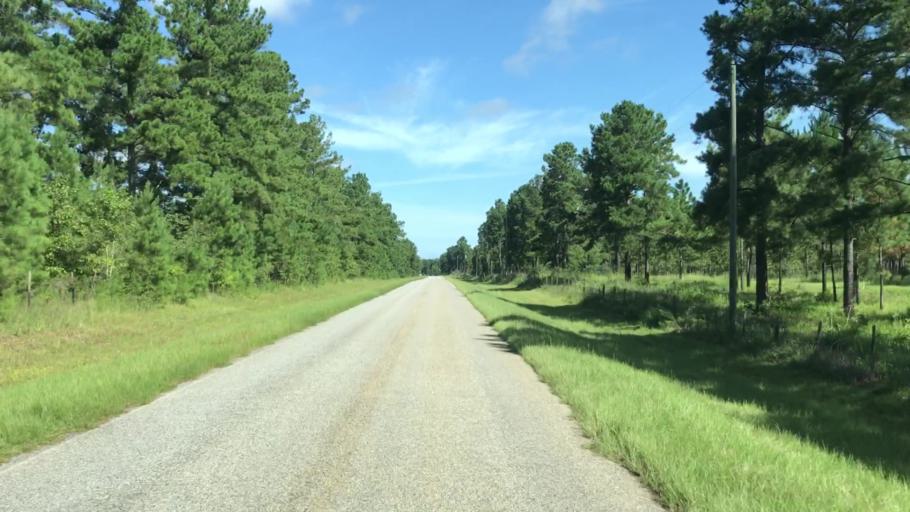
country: US
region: Georgia
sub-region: Jefferson County
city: Wadley
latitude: 32.8049
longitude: -82.3697
